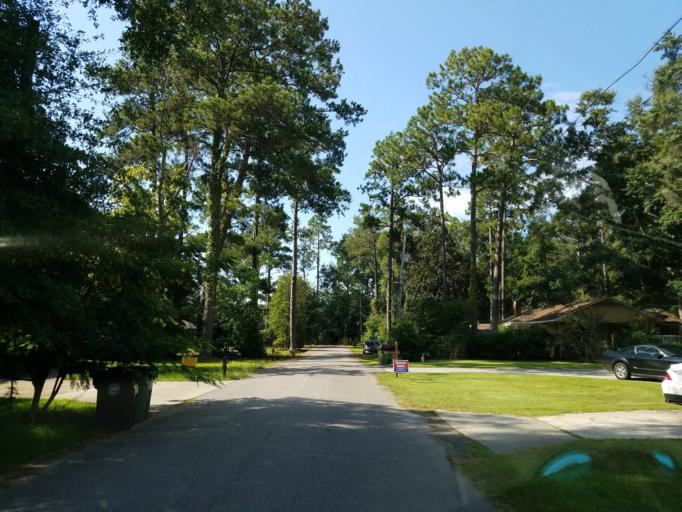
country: US
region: Mississippi
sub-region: Lamar County
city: West Hattiesburg
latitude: 31.3054
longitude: -89.3328
